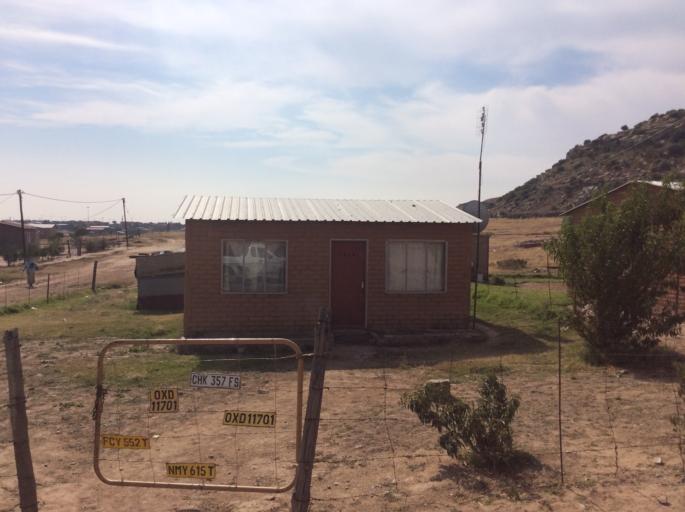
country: ZA
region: Orange Free State
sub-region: Xhariep District Municipality
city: Dewetsdorp
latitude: -29.5932
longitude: 26.6836
